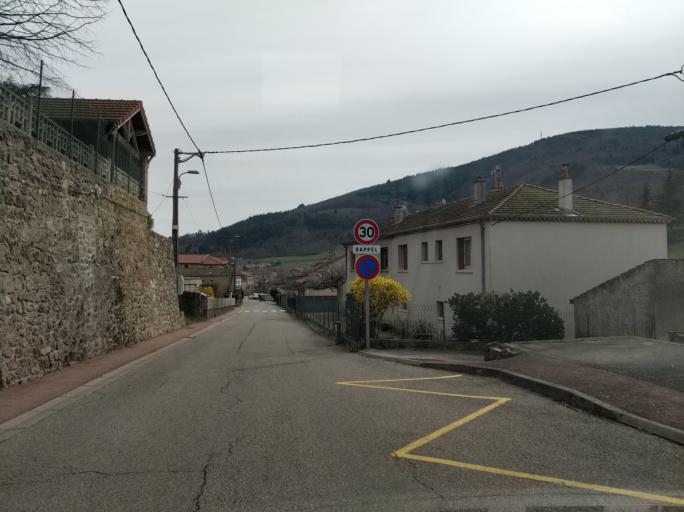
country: FR
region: Rhone-Alpes
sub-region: Departement de l'Ardeche
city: Satillieu
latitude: 45.1519
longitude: 4.6113
